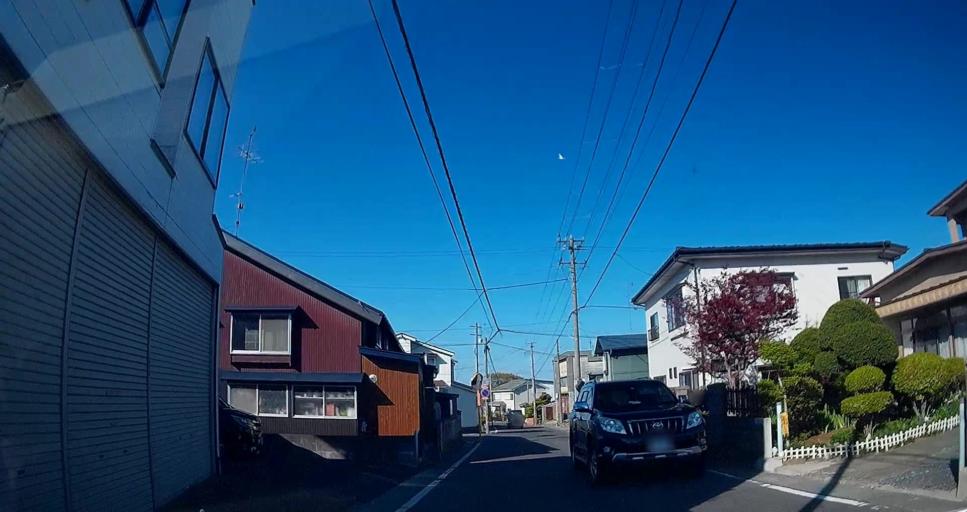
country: JP
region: Aomori
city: Hachinohe
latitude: 40.5255
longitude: 141.5487
